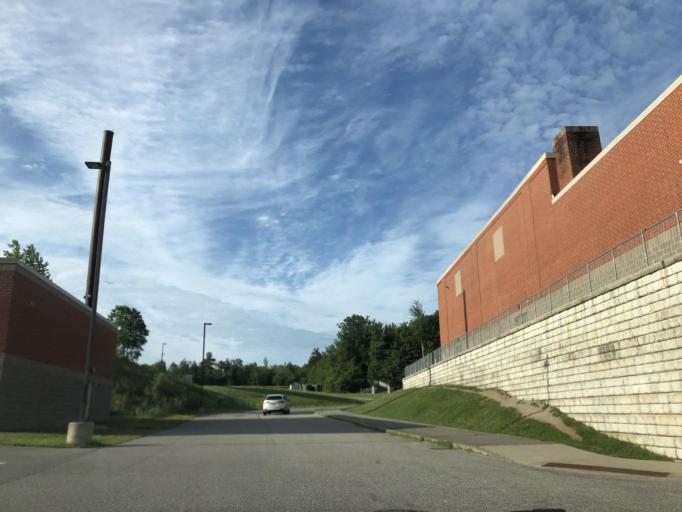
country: US
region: New Hampshire
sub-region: Merrimack County
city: Sutton
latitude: 43.3465
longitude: -71.9293
